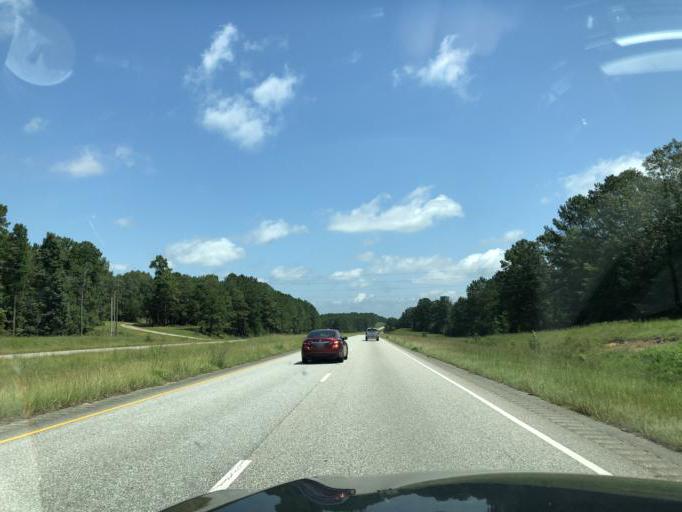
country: US
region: Alabama
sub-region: Henry County
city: Abbeville
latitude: 31.7418
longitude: -85.2442
